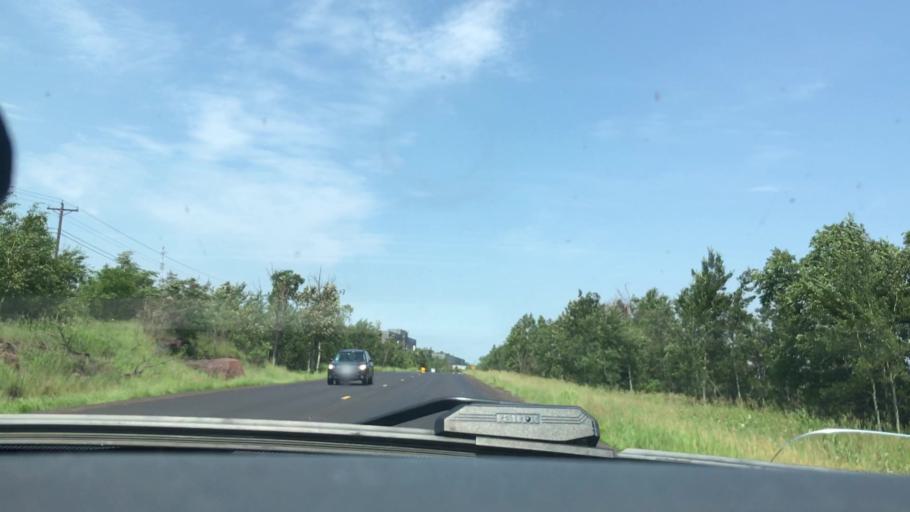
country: US
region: Minnesota
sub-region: Lake County
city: Silver Bay
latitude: 47.2834
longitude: -91.2684
